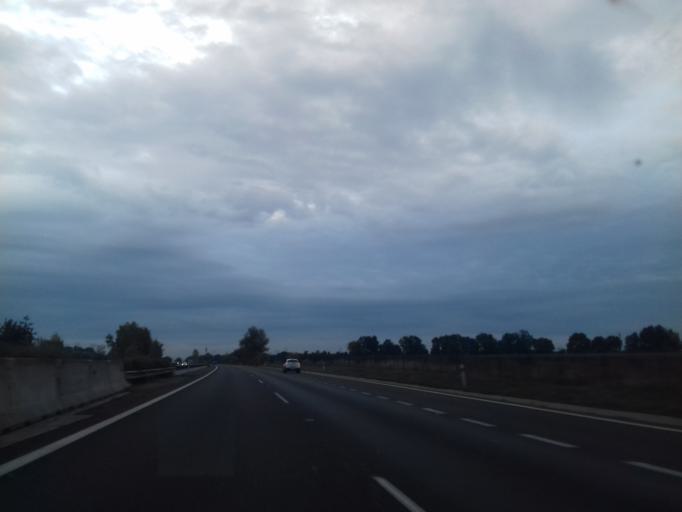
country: CZ
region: Central Bohemia
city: Poricany
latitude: 50.1183
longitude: 14.9454
